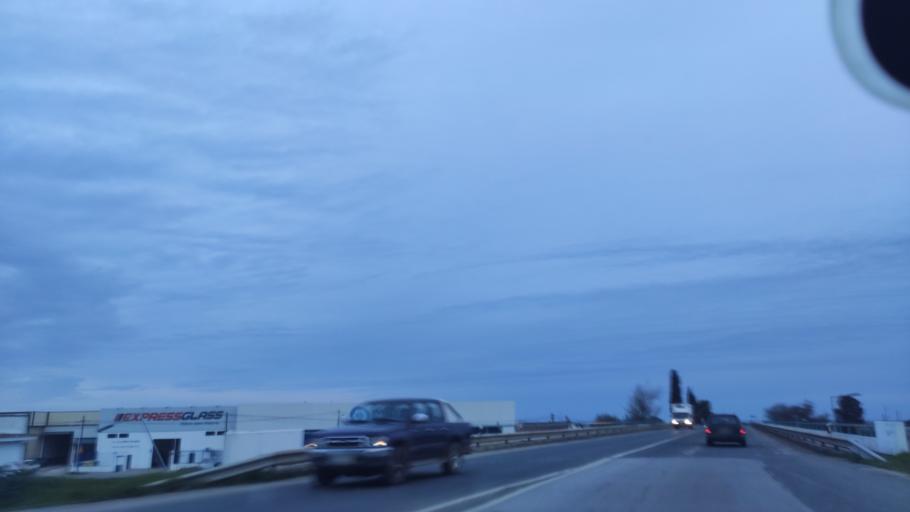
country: PT
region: Beja
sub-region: Beja
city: Beja
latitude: 38.0252
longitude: -7.8610
